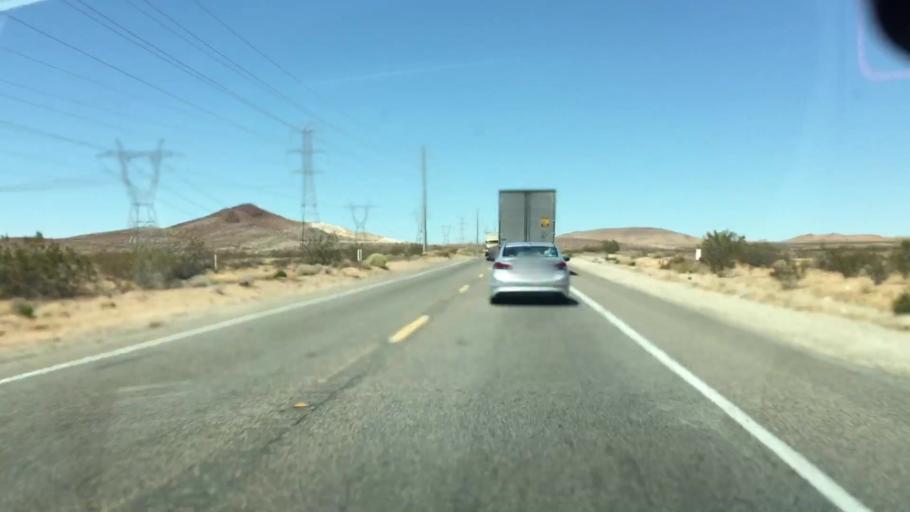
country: US
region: California
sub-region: Kern County
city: Boron
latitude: 34.8547
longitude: -117.5034
